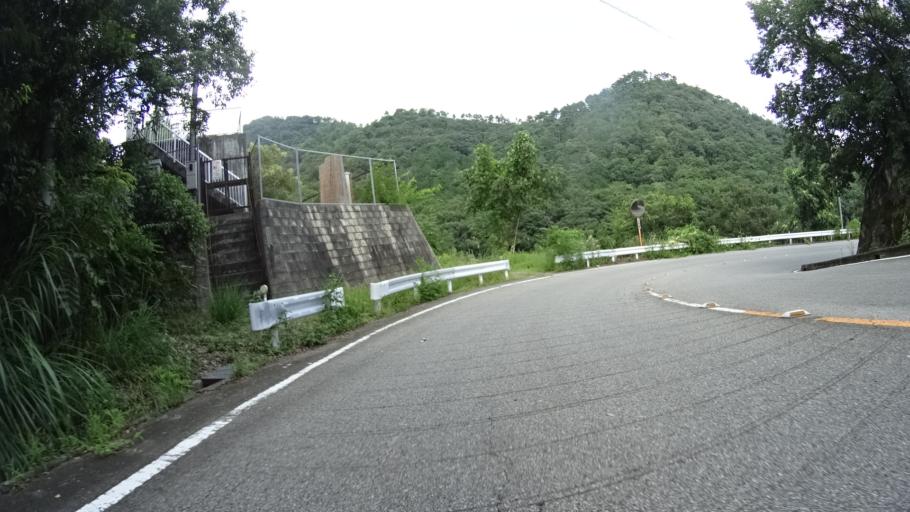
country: JP
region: Yamanashi
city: Kofu-shi
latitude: 35.6932
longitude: 138.5607
